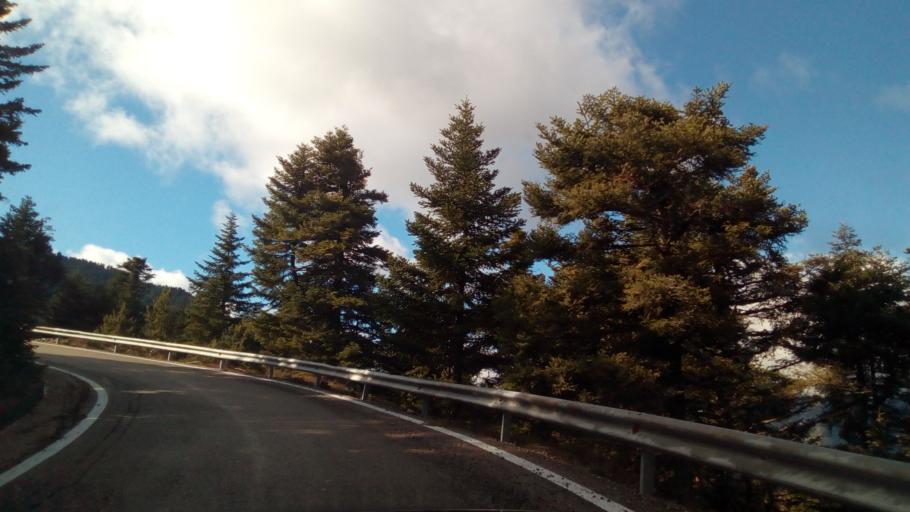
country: GR
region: West Greece
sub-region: Nomos Aitolias kai Akarnanias
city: Nafpaktos
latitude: 38.5864
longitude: 21.9371
